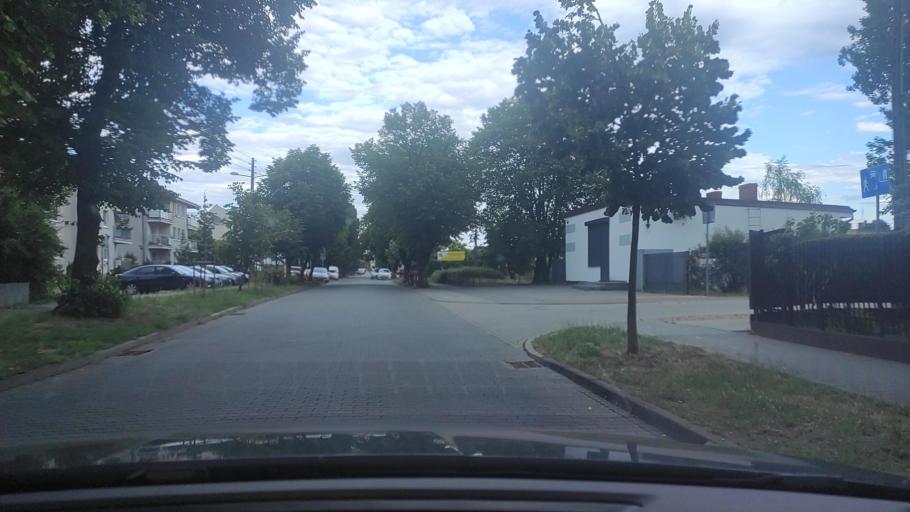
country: PL
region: Greater Poland Voivodeship
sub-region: Powiat poznanski
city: Swarzedz
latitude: 52.3982
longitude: 17.0503
